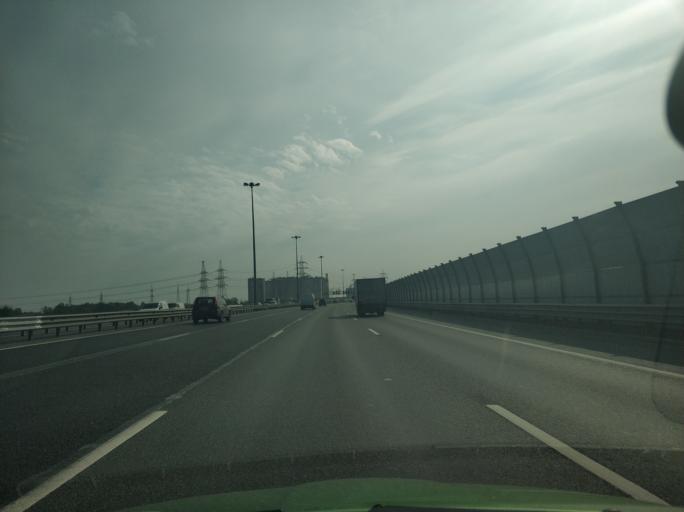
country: RU
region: St.-Petersburg
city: Grazhdanka
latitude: 60.0470
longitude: 30.4263
